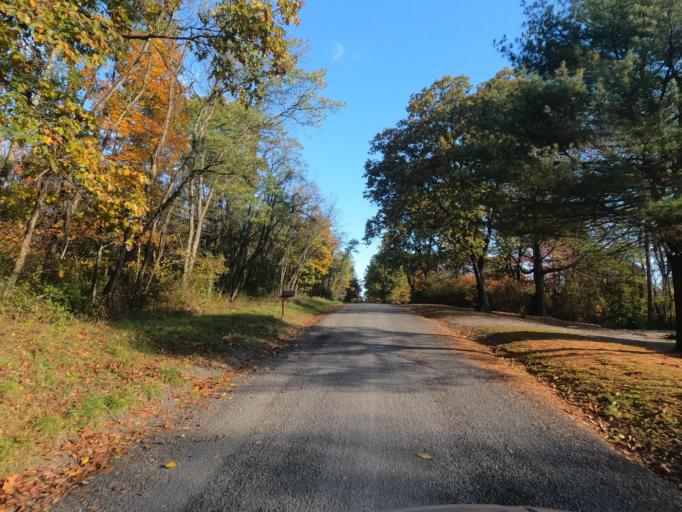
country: US
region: West Virginia
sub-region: Morgan County
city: Berkeley Springs
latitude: 39.6183
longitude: -78.4887
